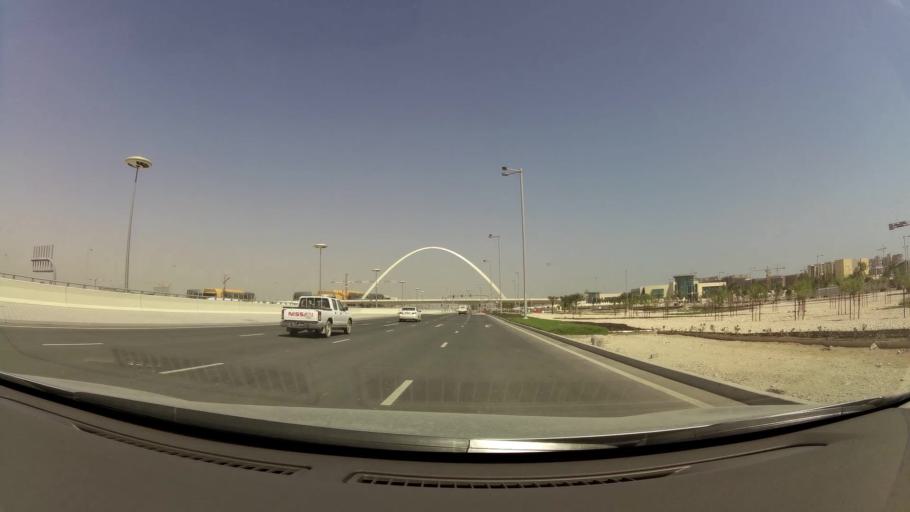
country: QA
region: Baladiyat Umm Salal
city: Umm Salal Muhammad
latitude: 25.3965
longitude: 51.5165
